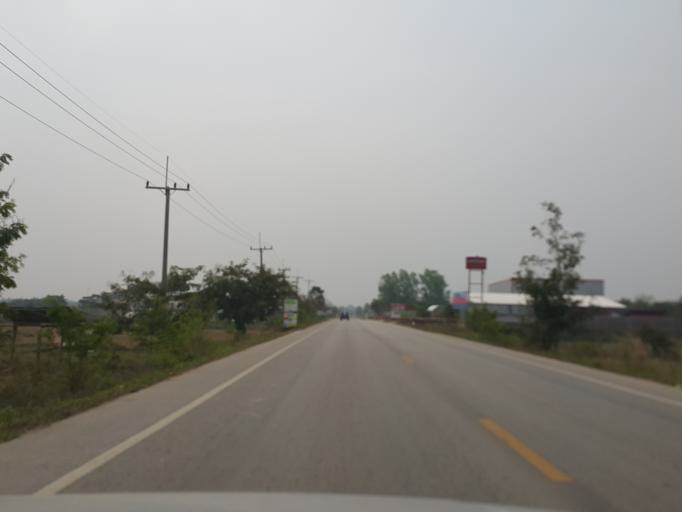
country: TH
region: Lampang
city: Ko Kha
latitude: 18.2152
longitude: 99.3938
